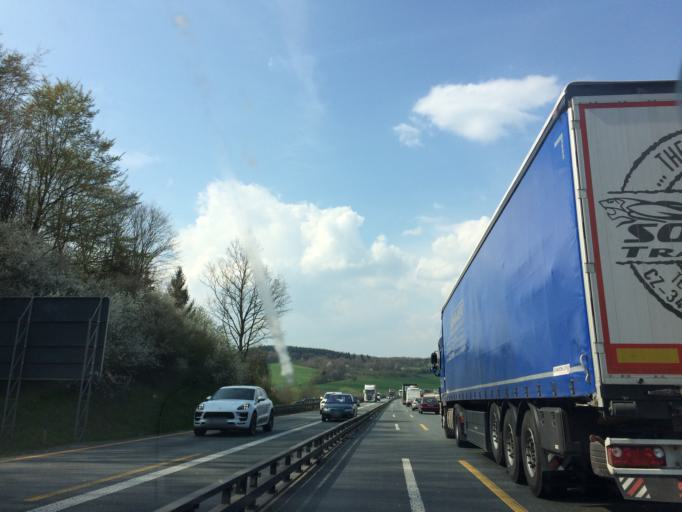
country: DE
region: Hesse
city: Allendorf an der Lahn
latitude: 50.5449
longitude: 8.5723
